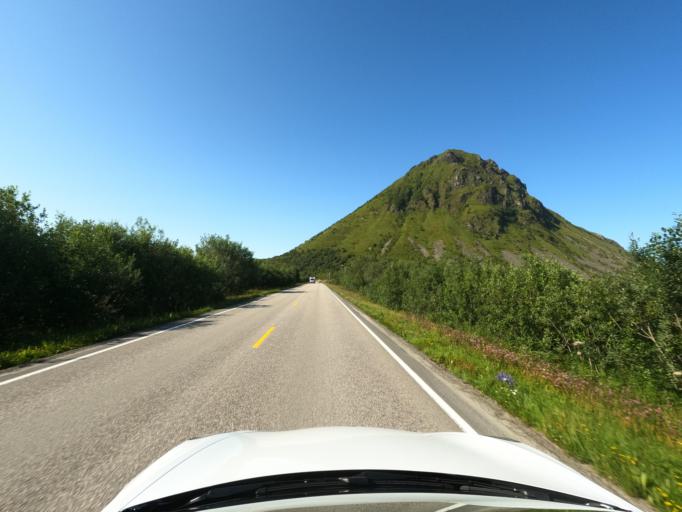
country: NO
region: Nordland
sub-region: Vestvagoy
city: Evjen
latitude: 68.2706
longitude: 13.9725
